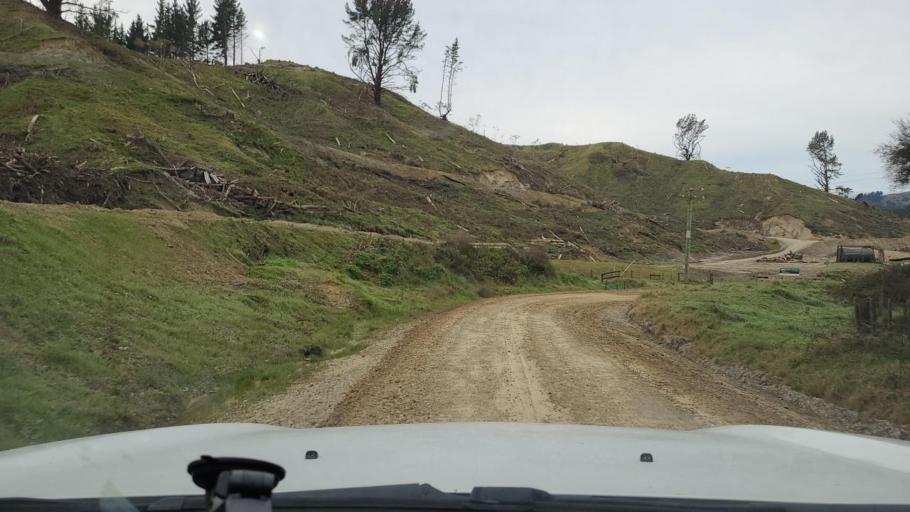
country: NZ
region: Gisborne
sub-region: Gisborne District
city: Gisborne
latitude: -38.5730
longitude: 178.0378
